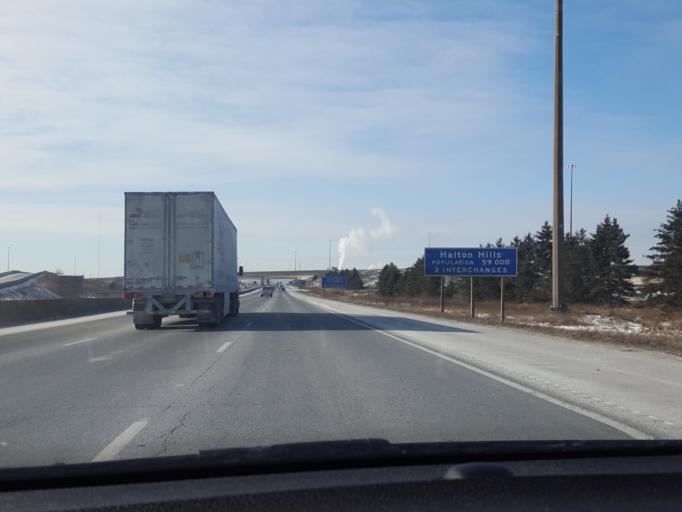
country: CA
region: Ontario
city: Brampton
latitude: 43.5947
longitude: -79.8032
